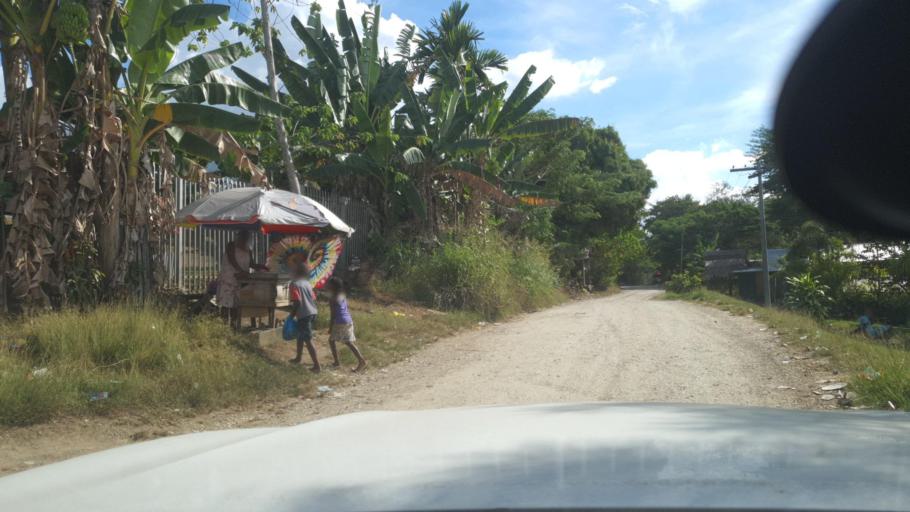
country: SB
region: Guadalcanal
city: Honiara
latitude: -9.4381
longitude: 159.9483
